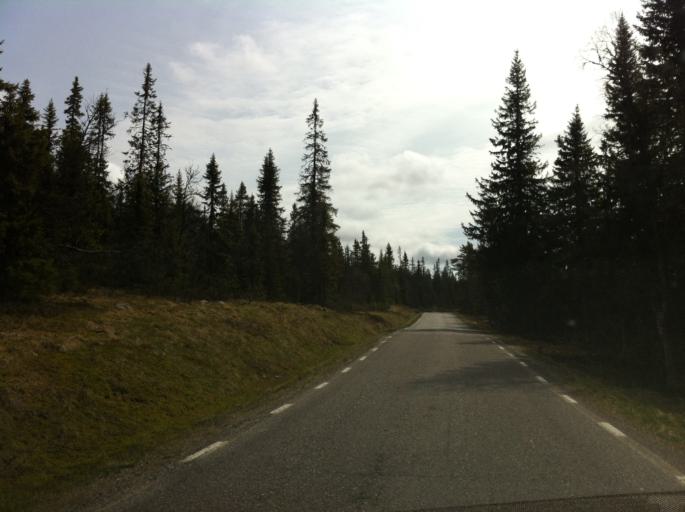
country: NO
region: Hedmark
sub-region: Engerdal
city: Engerdal
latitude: 62.3024
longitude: 12.8010
